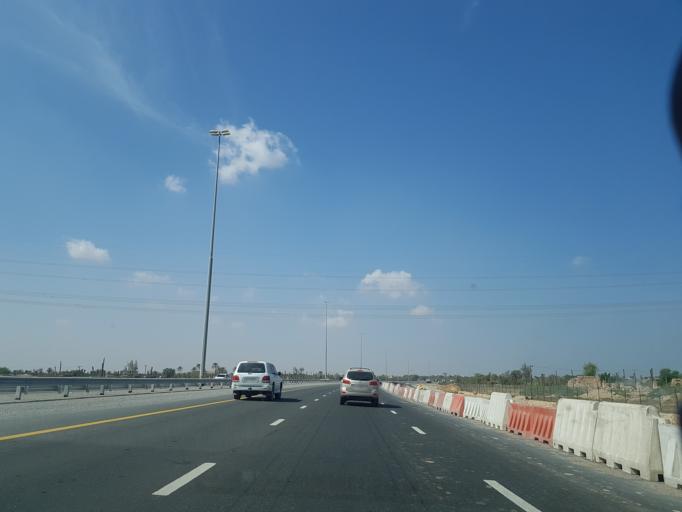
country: AE
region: Ra's al Khaymah
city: Ras al-Khaimah
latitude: 25.6979
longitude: 55.9827
